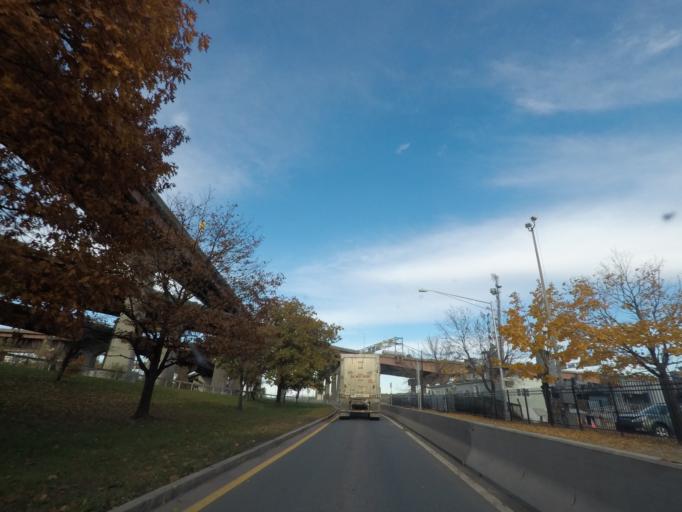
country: US
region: New York
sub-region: Rensselaer County
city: Rensselaer
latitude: 42.6424
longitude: -73.7506
